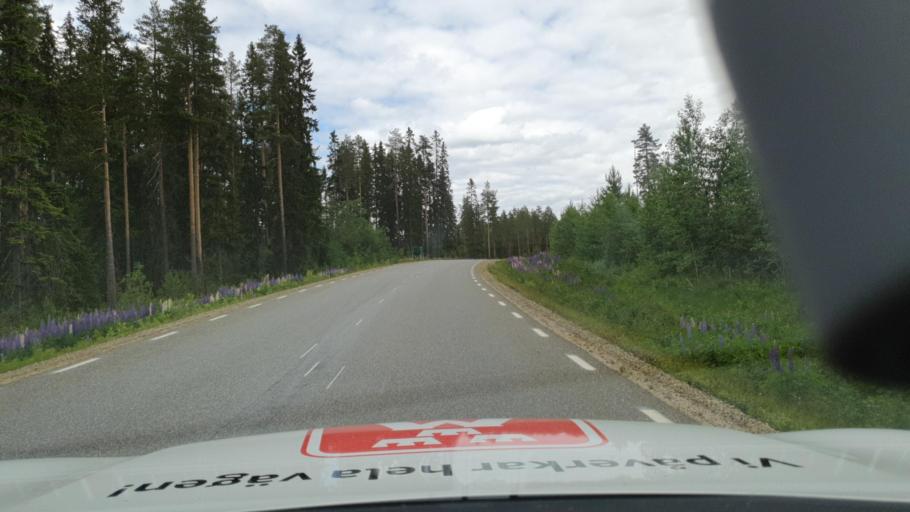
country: SE
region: Vaesterbotten
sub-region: Bjurholms Kommun
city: Bjurholm
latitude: 63.8747
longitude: 18.9844
